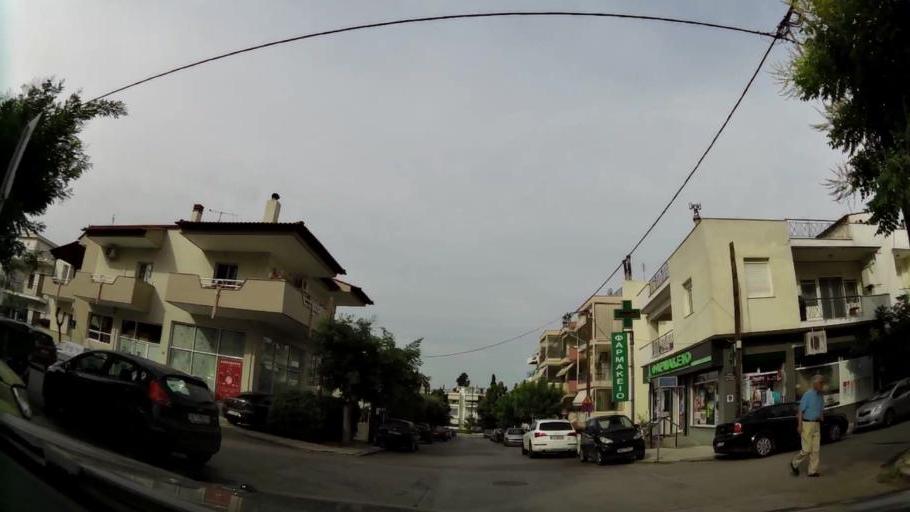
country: GR
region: Central Macedonia
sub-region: Nomos Thessalonikis
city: Thermi
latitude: 40.5466
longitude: 23.0179
